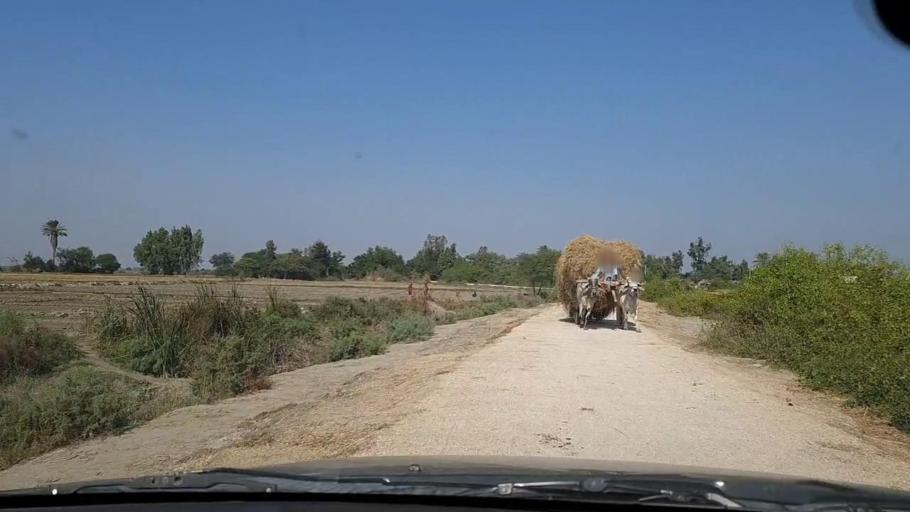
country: PK
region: Sindh
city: Chuhar Jamali
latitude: 24.3962
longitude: 67.8236
